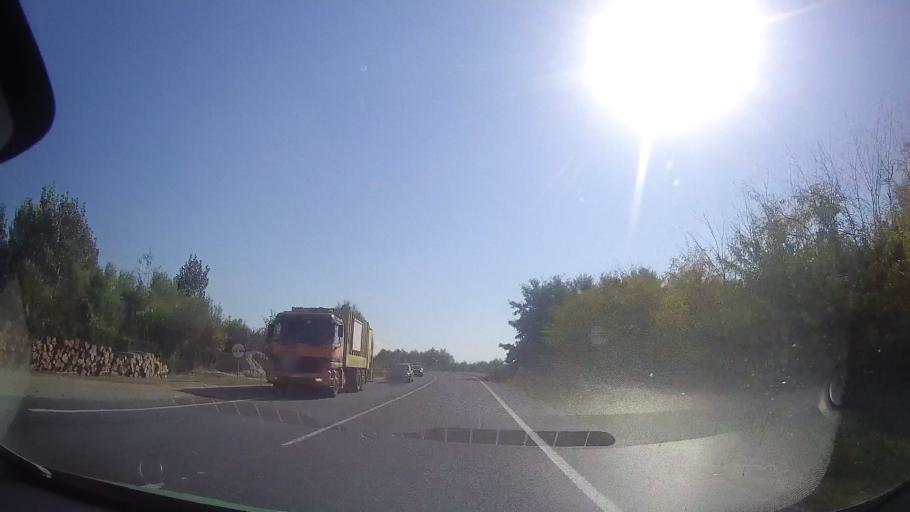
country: RO
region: Timis
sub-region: Comuna Costeiu
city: Costeiu
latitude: 45.7384
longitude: 21.8434
